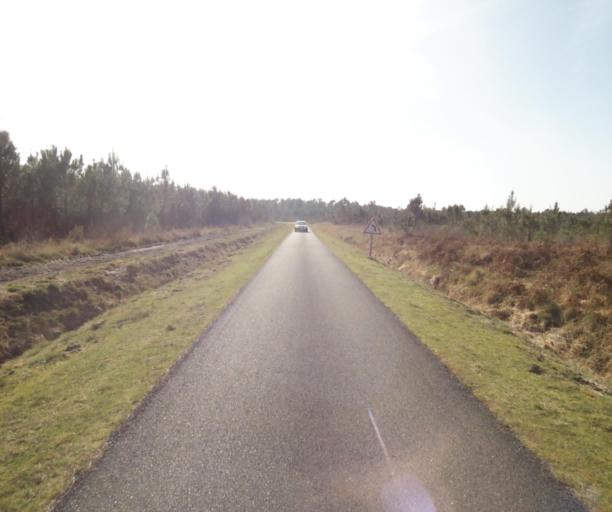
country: FR
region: Aquitaine
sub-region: Departement des Landes
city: Roquefort
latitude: 44.2108
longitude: -0.2527
